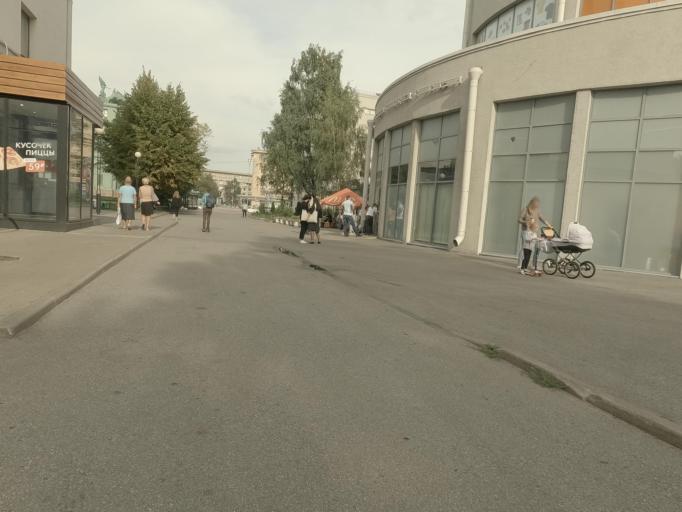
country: RU
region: St.-Petersburg
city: Admiralteisky
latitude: 59.9002
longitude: 30.2718
